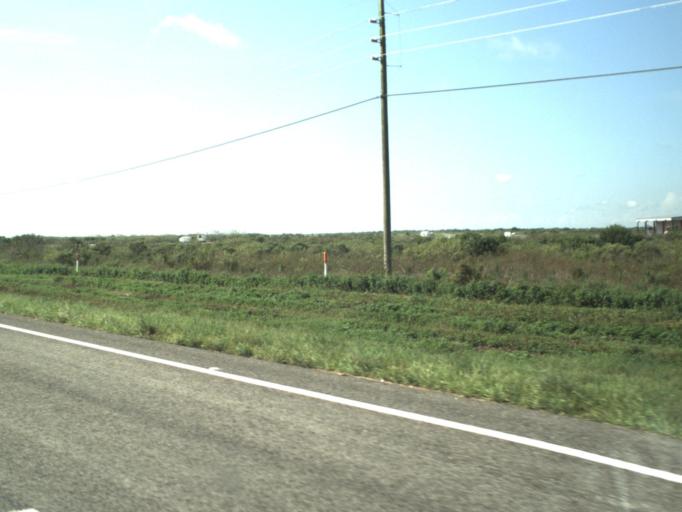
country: US
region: Florida
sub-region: Palm Beach County
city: Belle Glade Camp
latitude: 26.4884
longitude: -80.6569
